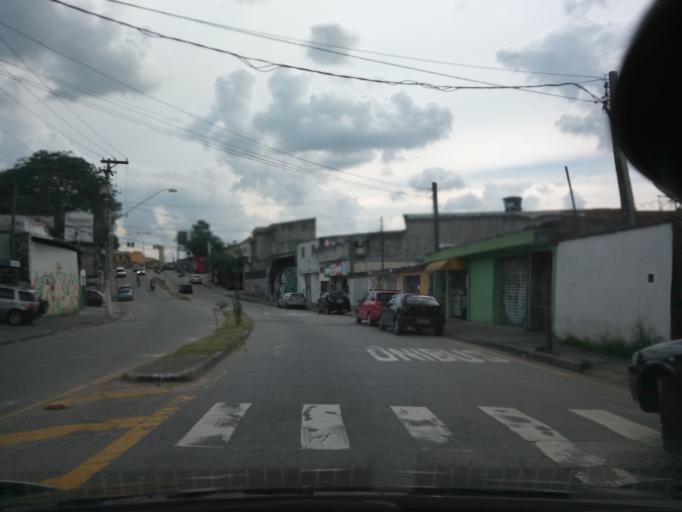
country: BR
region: Sao Paulo
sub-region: Sao Bernardo Do Campo
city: Sao Bernardo do Campo
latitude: -23.7415
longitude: -46.5748
